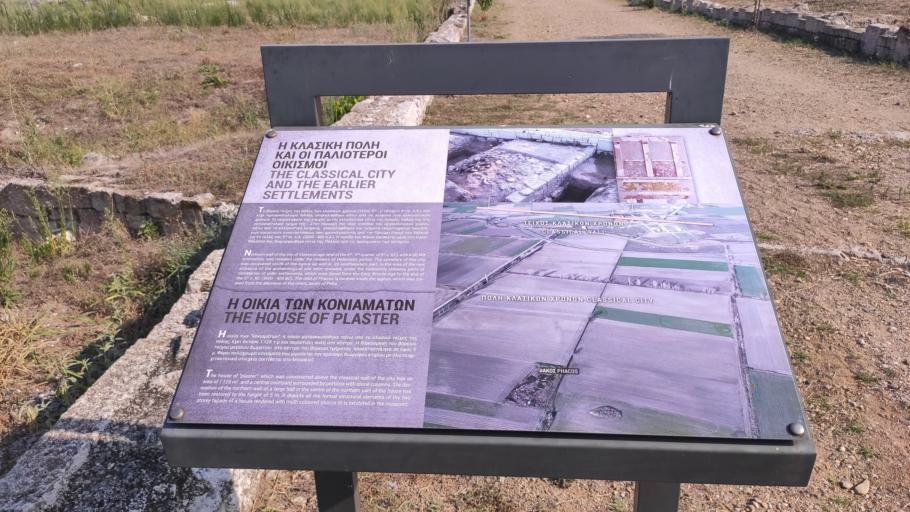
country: GR
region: Central Macedonia
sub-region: Nomos Pellis
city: Pella
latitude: 40.7528
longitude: 22.5179
